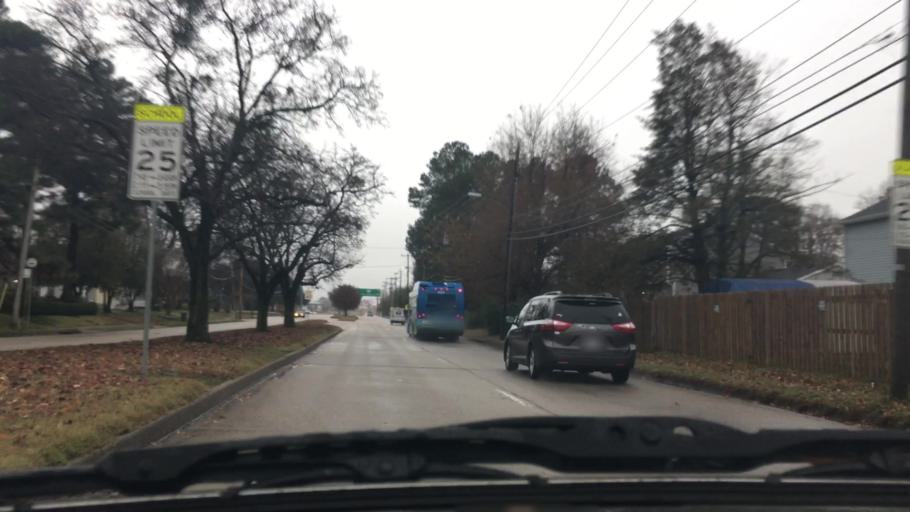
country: US
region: Virginia
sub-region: City of Norfolk
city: Norfolk
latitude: 36.9210
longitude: -76.2531
